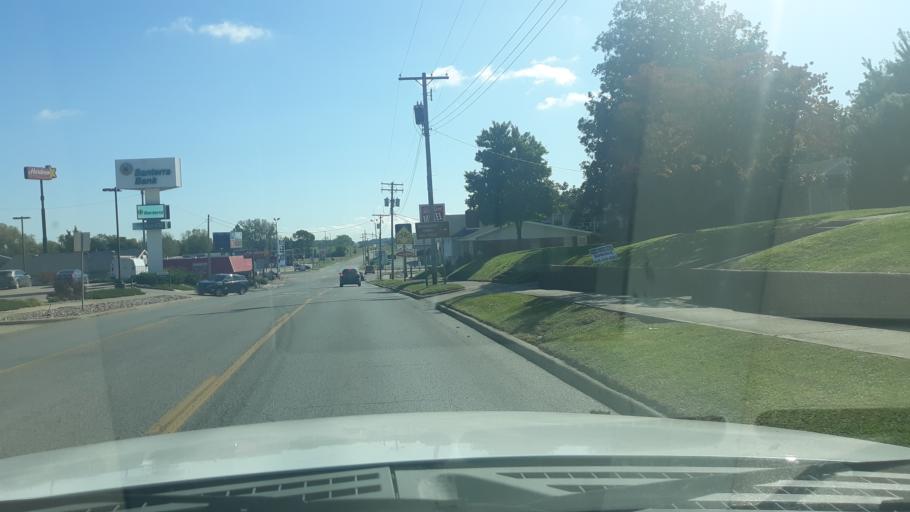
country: US
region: Illinois
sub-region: Saline County
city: Harrisburg
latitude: 37.7383
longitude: -88.5351
